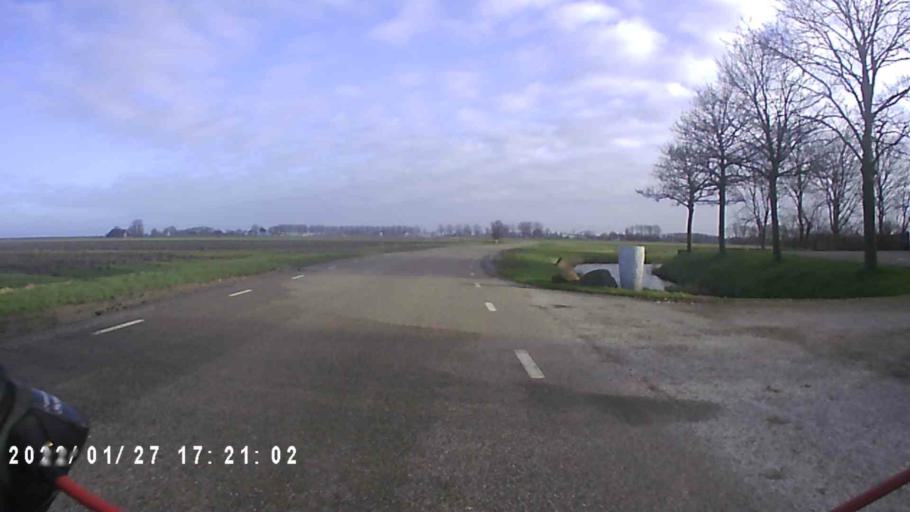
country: NL
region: Friesland
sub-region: Gemeente Dongeradeel
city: Anjum
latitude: 53.3827
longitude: 6.1184
